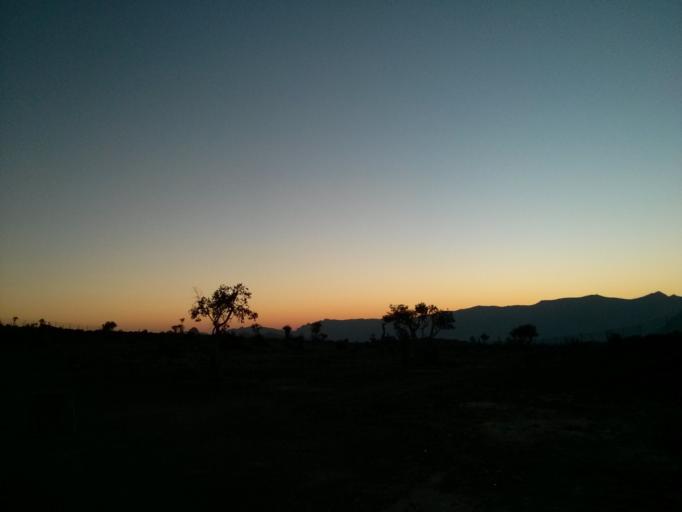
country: OM
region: Muhafazat ad Dakhiliyah
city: Bahla'
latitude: 23.2087
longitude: 57.1969
